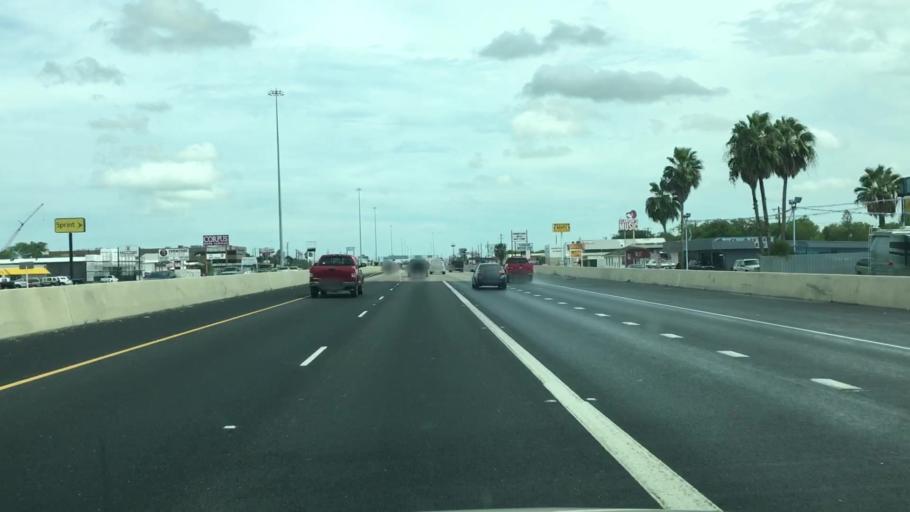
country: US
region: Texas
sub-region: Nueces County
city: Corpus Christi
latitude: 27.7335
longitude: -97.4232
